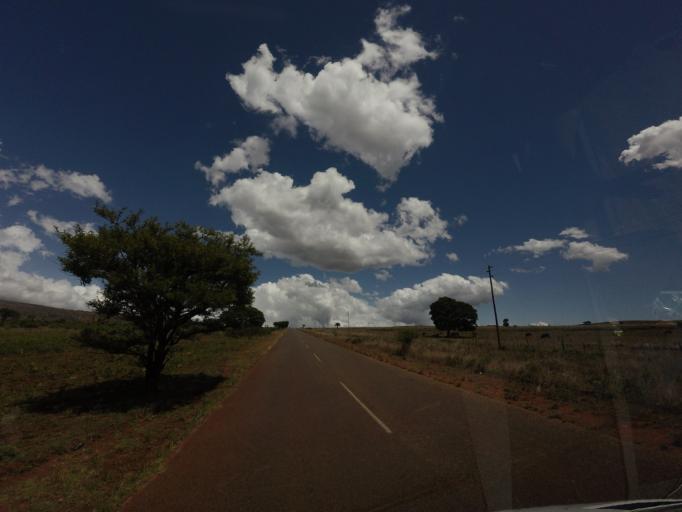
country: ZA
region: Limpopo
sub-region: Mopani District Municipality
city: Hoedspruit
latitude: -24.6134
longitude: 30.8161
